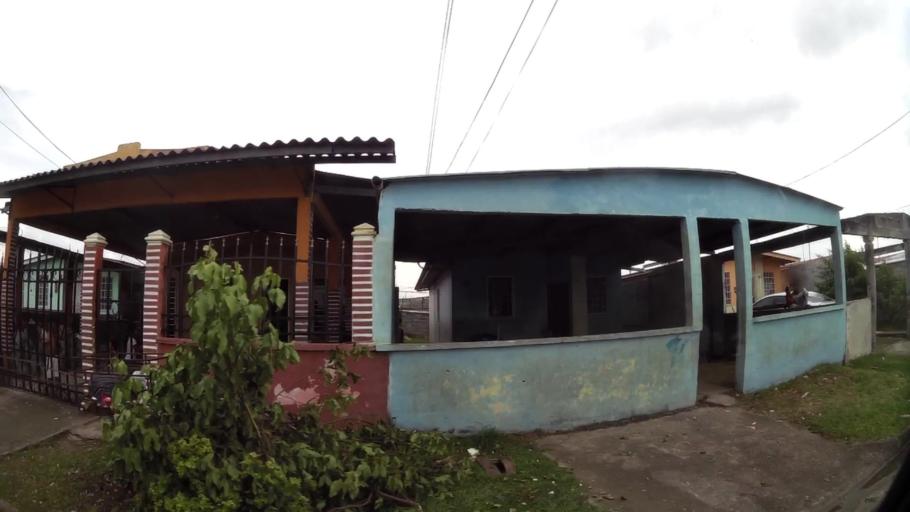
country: PA
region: Panama
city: Cabra Numero Uno
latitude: 9.0913
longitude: -79.3477
